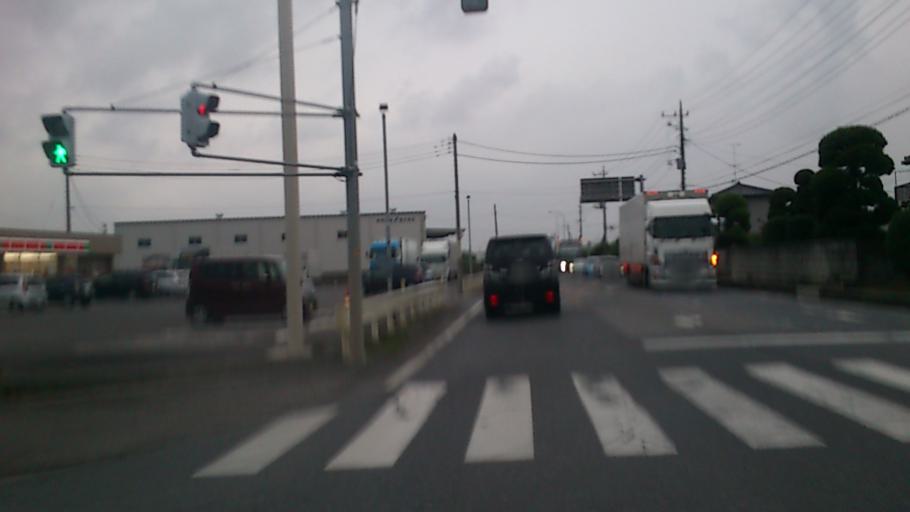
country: JP
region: Saitama
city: Kazo
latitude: 36.1630
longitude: 139.5977
